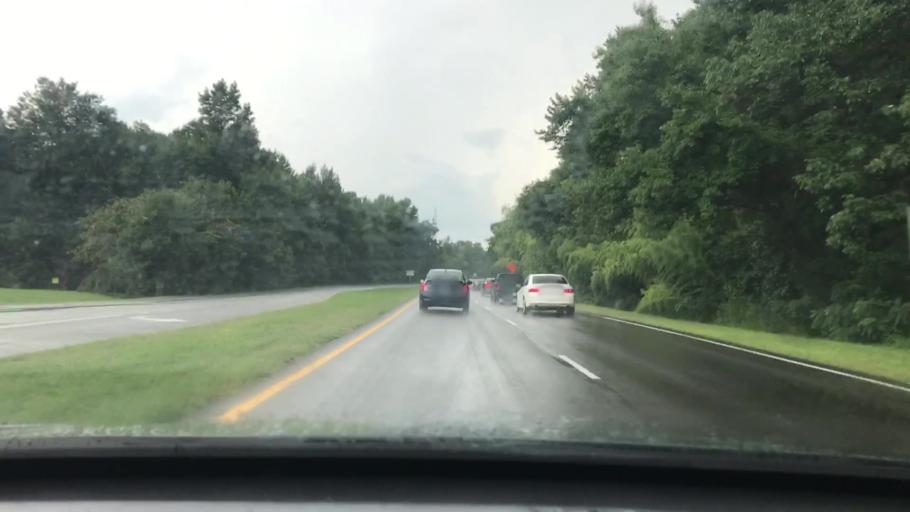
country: US
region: Virginia
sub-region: Henrico County
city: Laurel
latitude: 37.6297
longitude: -77.5199
